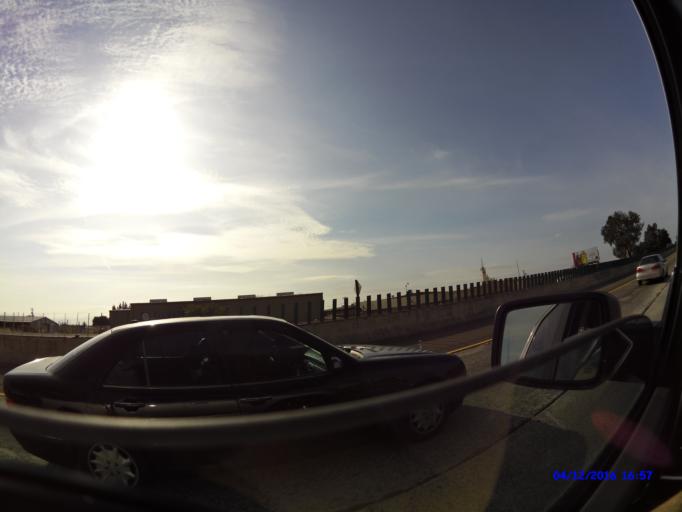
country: US
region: California
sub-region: Stanislaus County
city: Modesto
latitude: 37.6556
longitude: -121.0260
